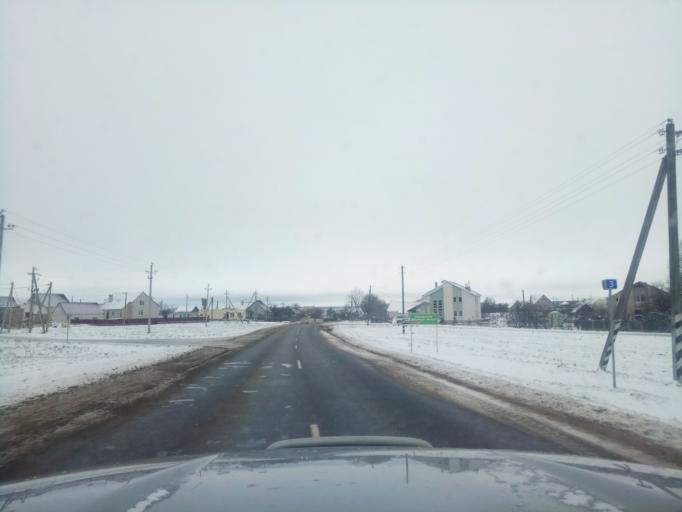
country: BY
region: Minsk
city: Kapyl'
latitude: 53.1574
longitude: 27.1013
